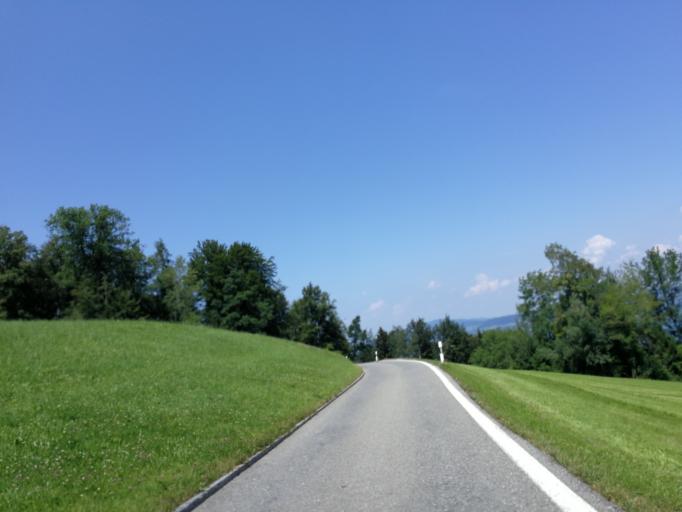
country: CH
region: Schwyz
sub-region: Bezirk Hoefe
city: Freienbach
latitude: 47.1869
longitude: 8.7861
